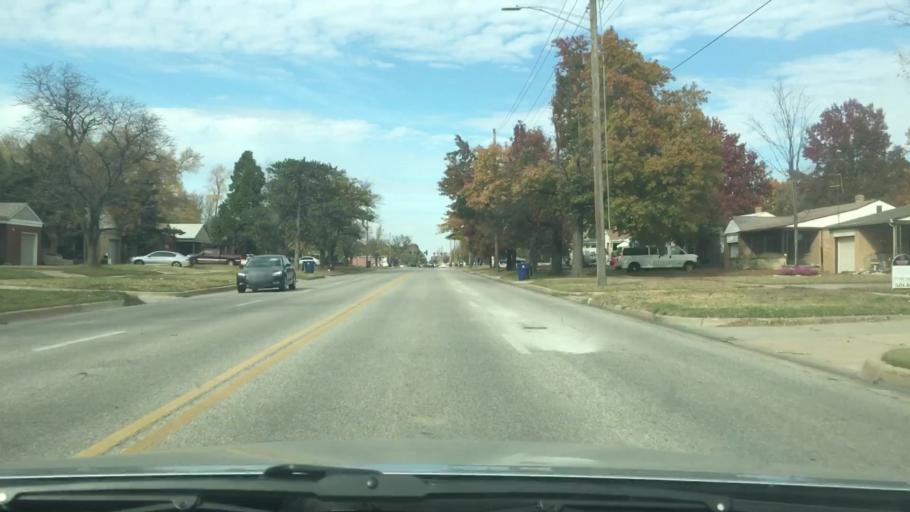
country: US
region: Kansas
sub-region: Sedgwick County
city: Wichita
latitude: 37.6612
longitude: -97.2621
